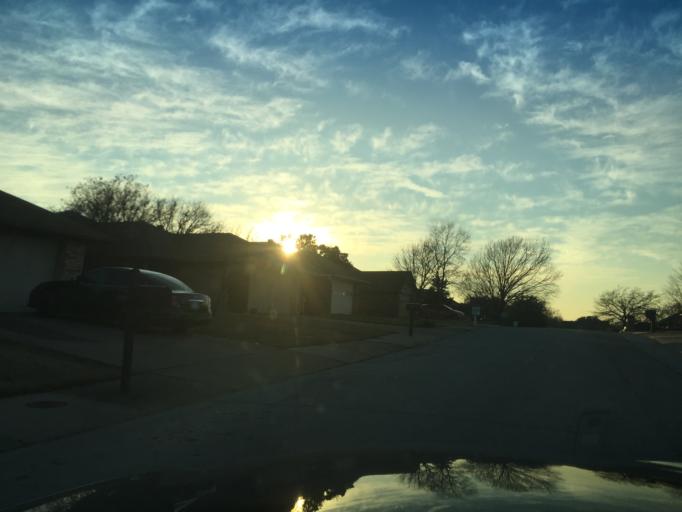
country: US
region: Texas
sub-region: Dallas County
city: Carrollton
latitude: 32.9897
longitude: -96.8777
